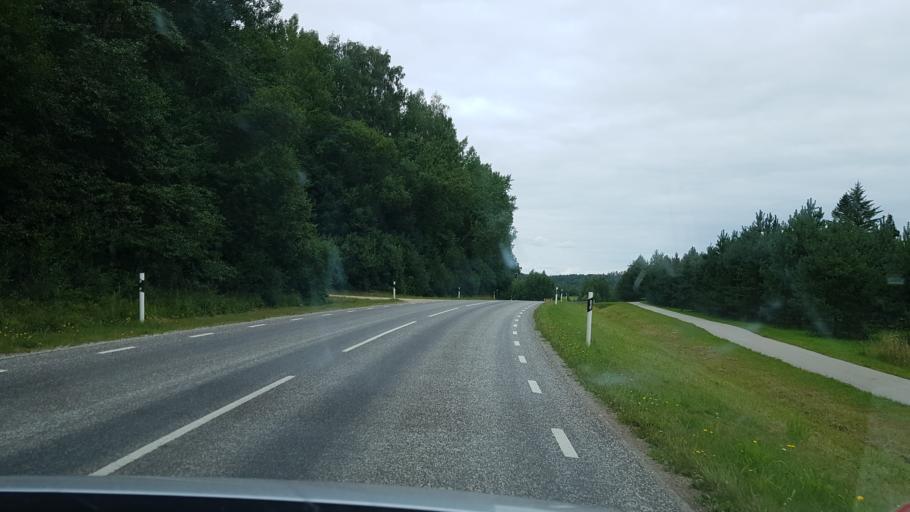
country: EE
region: Vorumaa
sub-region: Antsla vald
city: Vana-Antsla
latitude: 58.0455
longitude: 26.5467
